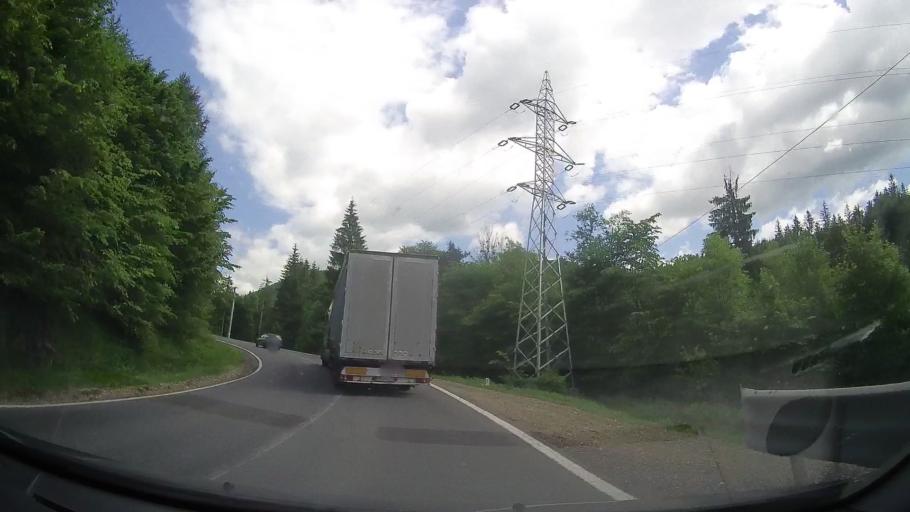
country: RO
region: Prahova
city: Maneciu
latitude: 45.3701
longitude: 25.9305
